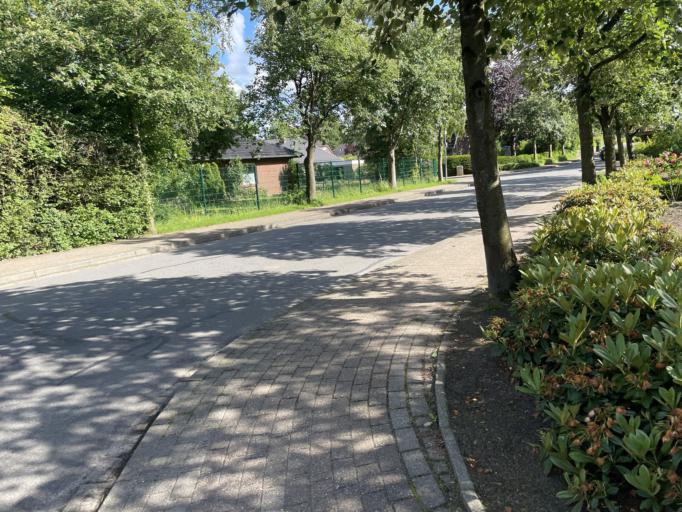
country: DE
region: Schleswig-Holstein
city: Mildstedt
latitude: 54.4655
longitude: 9.0993
